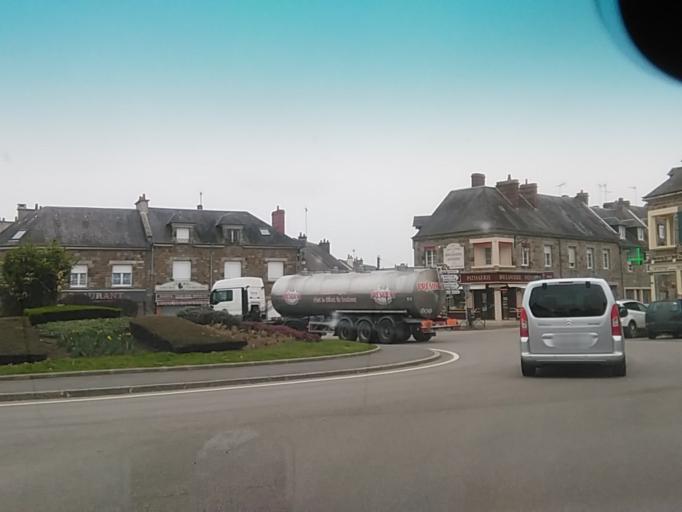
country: FR
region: Lower Normandy
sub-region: Departement de l'Orne
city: Ecouche
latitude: 48.6404
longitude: -0.2109
